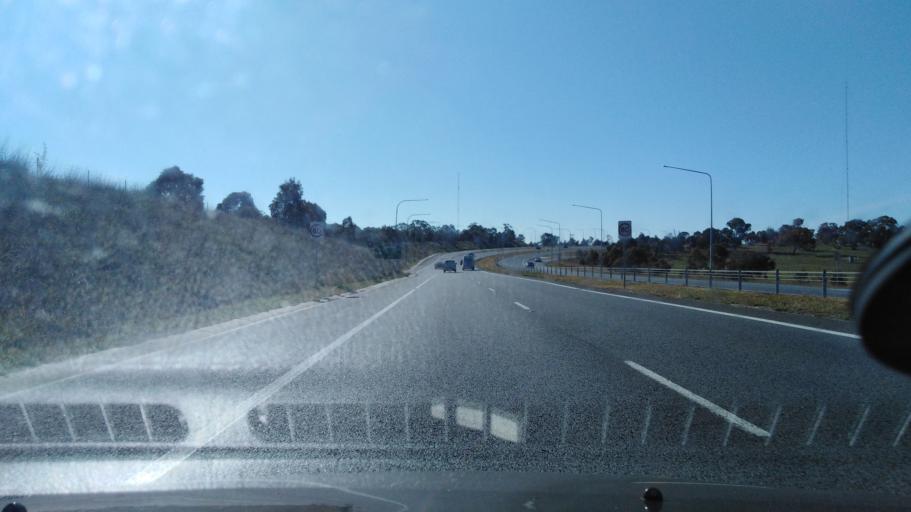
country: AU
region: Australian Capital Territory
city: Kaleen
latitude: -35.2308
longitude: 149.1183
